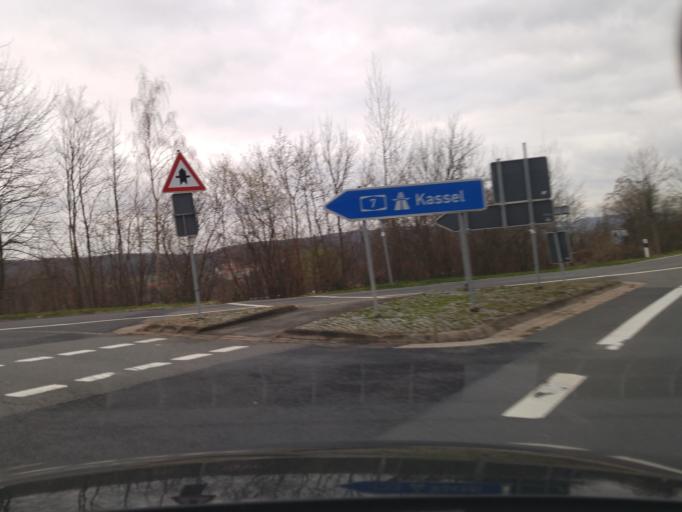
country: DE
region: Lower Saxony
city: Holle
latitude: 52.1030
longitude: 10.1449
